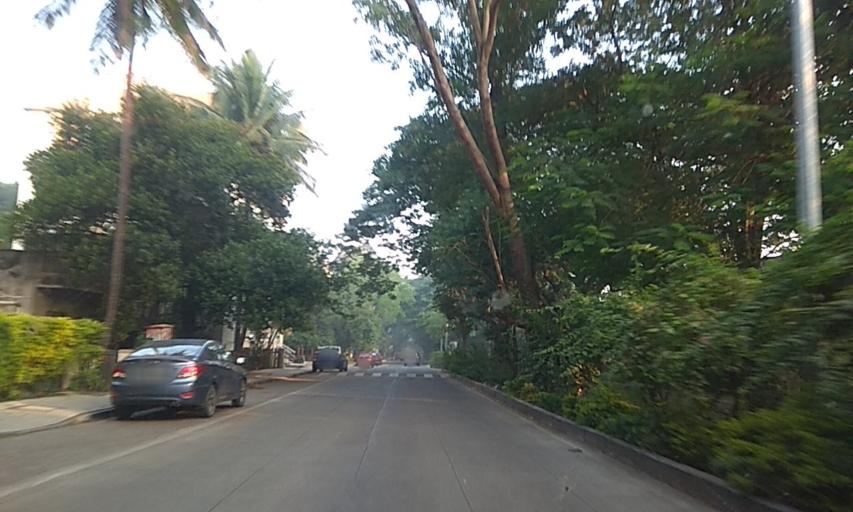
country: IN
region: Maharashtra
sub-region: Pune Division
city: Shivaji Nagar
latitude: 18.5431
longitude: 73.8173
